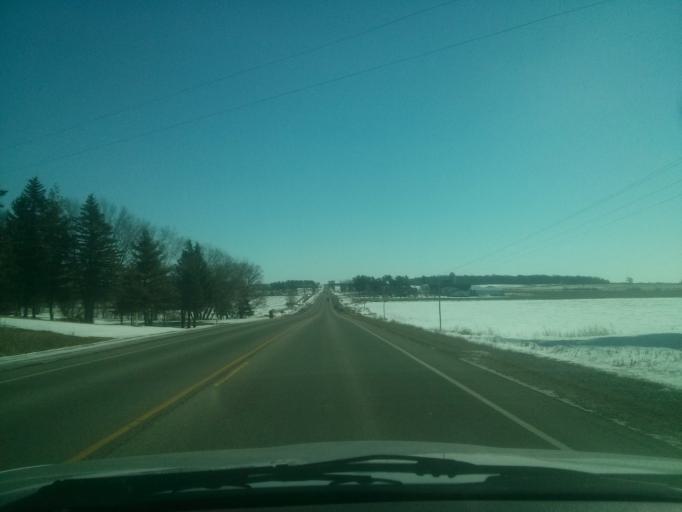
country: US
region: Wisconsin
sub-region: Saint Croix County
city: New Richmond
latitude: 45.1370
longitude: -92.4611
